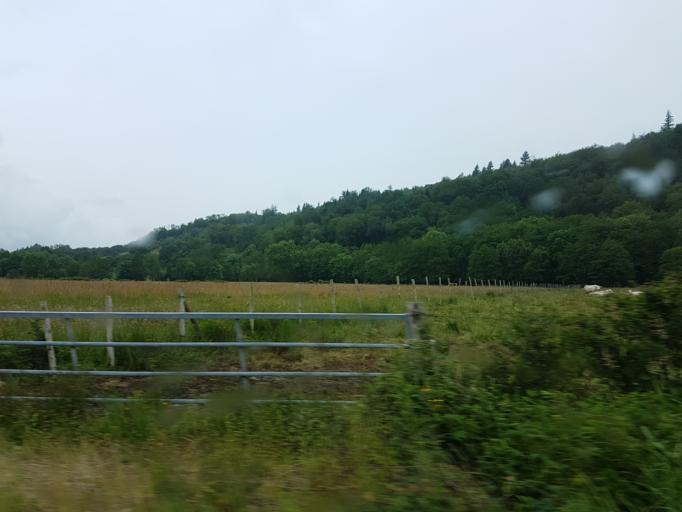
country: FR
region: Bourgogne
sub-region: Departement de la Nievre
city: Lormes
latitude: 47.1787
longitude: 3.7811
